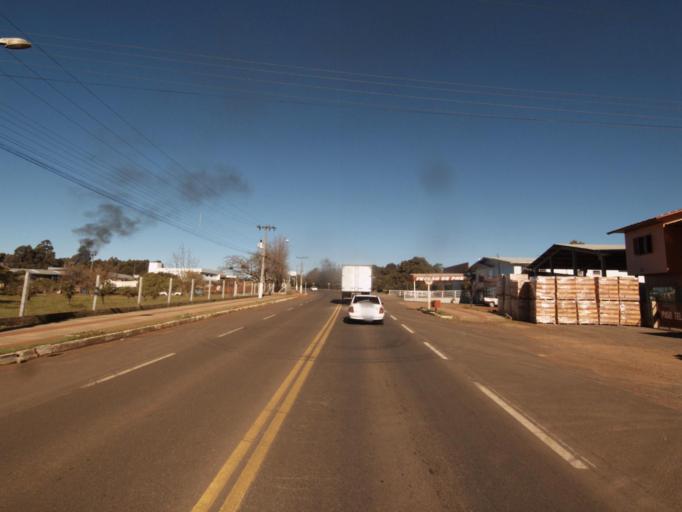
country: AR
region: Misiones
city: Bernardo de Irigoyen
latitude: -26.7590
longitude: -53.5028
